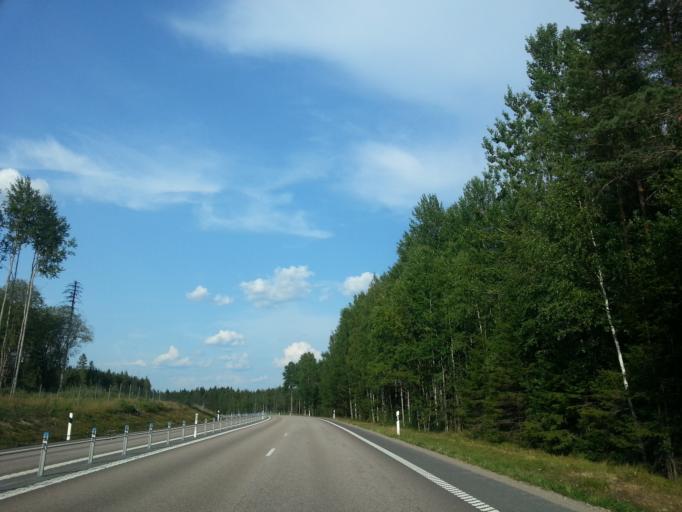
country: SE
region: Vaestmanland
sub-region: Norbergs Kommun
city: Norberg
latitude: 60.1060
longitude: 16.0341
